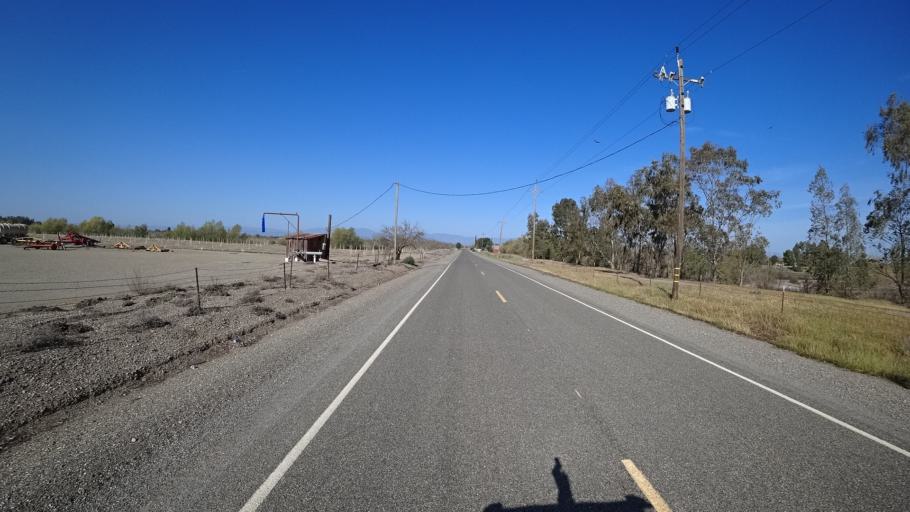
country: US
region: California
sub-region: Glenn County
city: Willows
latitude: 39.5533
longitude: -122.1592
